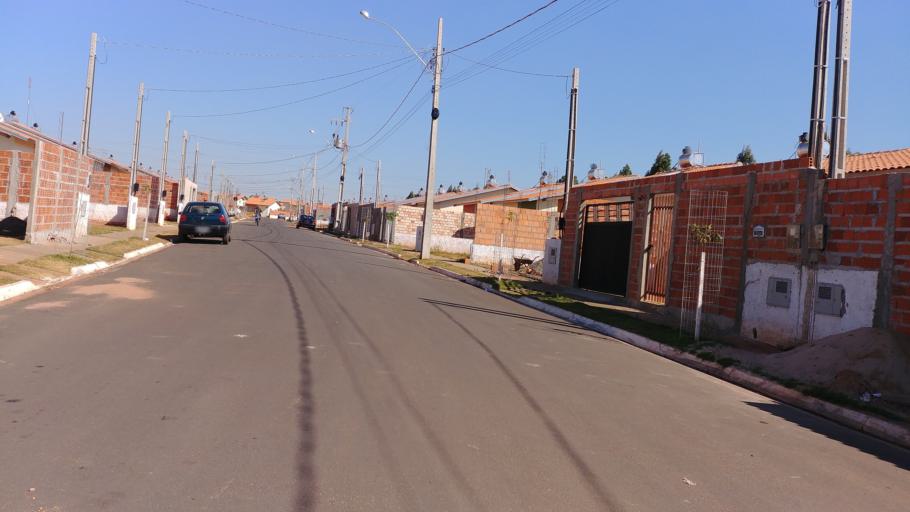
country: BR
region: Sao Paulo
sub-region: Paraguacu Paulista
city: Paraguacu Paulista
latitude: -22.4435
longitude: -50.5879
